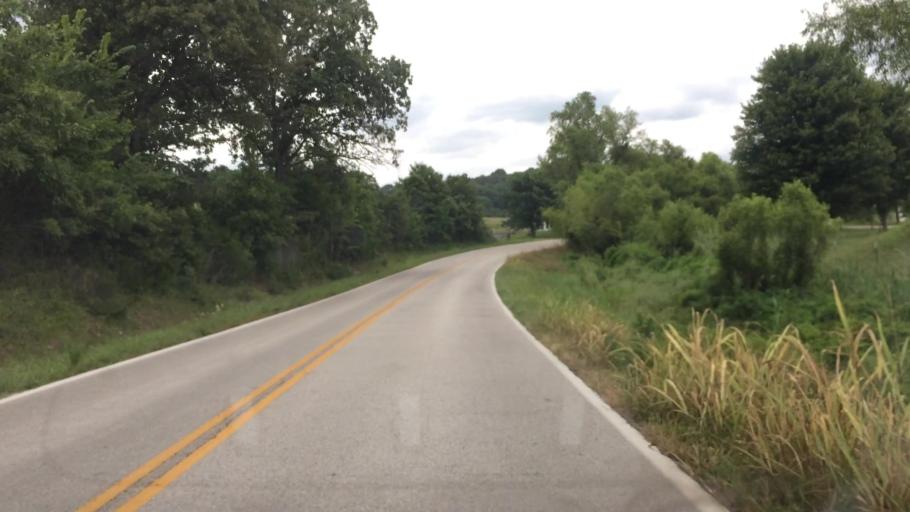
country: US
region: Missouri
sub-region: Greene County
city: Strafford
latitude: 37.2918
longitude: -93.0870
